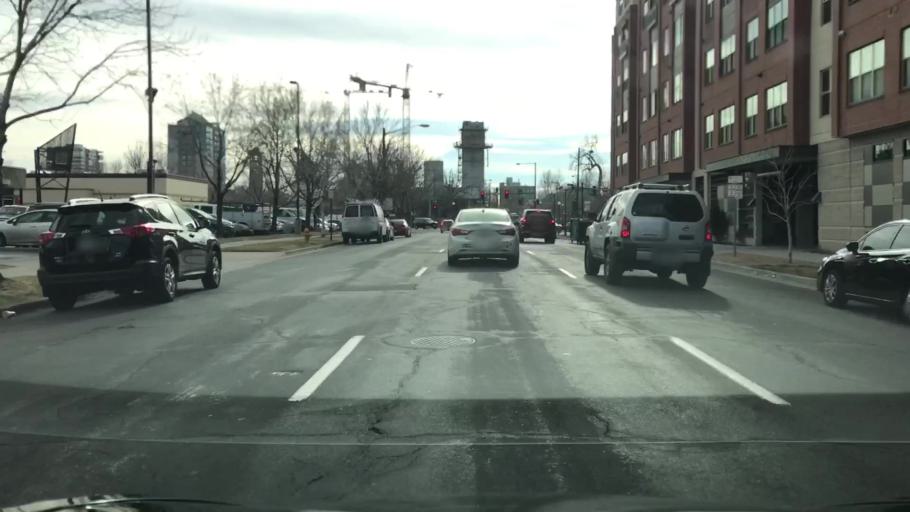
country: US
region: Colorado
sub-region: Denver County
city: Denver
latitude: 39.7253
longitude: -104.9837
